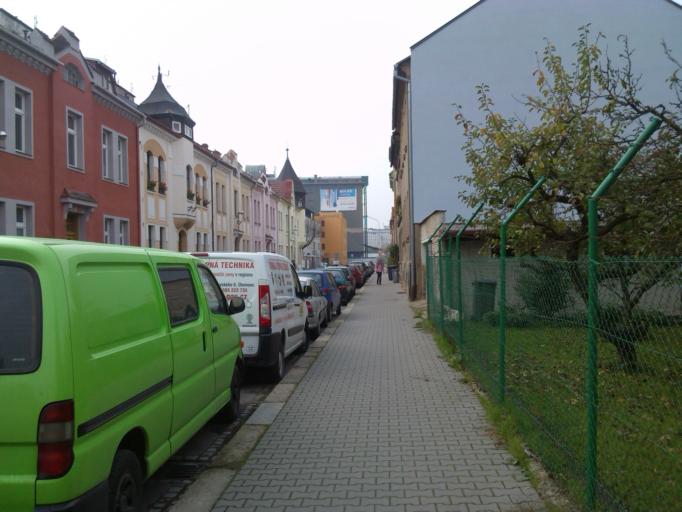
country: CZ
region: Olomoucky
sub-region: Okres Olomouc
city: Olomouc
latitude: 49.5832
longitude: 17.2510
